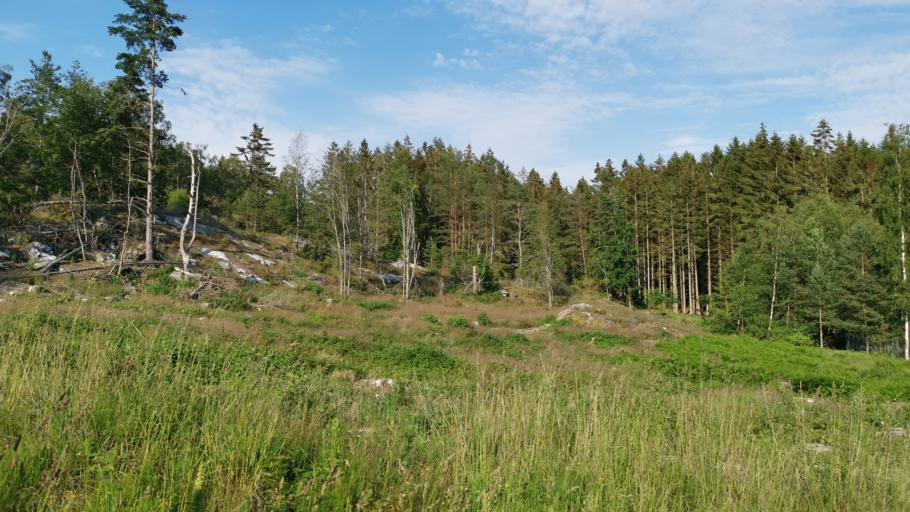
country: SE
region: Vaestra Goetaland
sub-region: Orust
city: Henan
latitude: 58.2896
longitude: 11.6475
